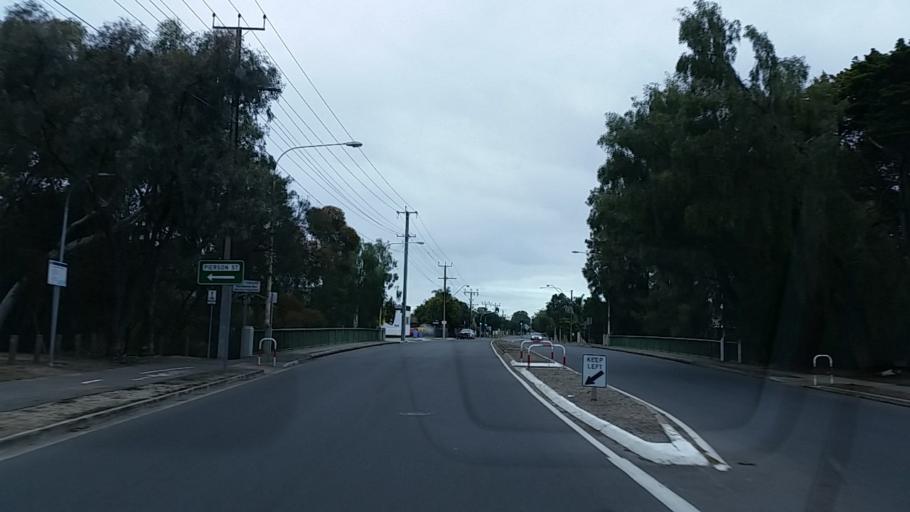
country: AU
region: South Australia
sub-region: Charles Sturt
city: Findon
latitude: -34.9180
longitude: 138.5351
